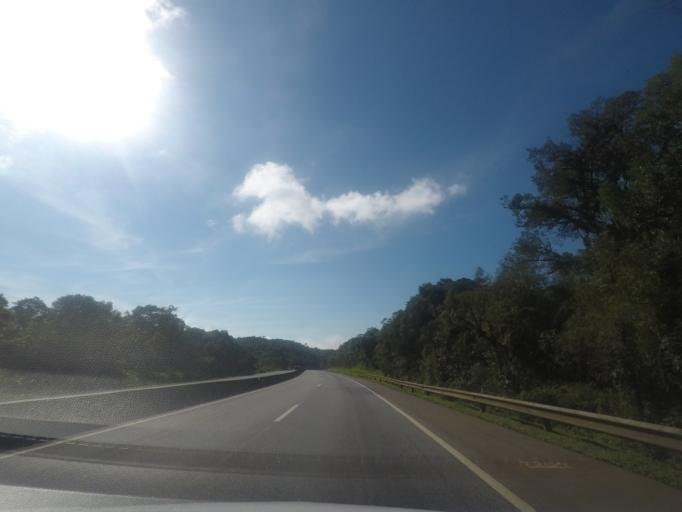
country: BR
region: Parana
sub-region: Piraquara
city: Piraquara
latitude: -25.5918
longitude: -48.9258
